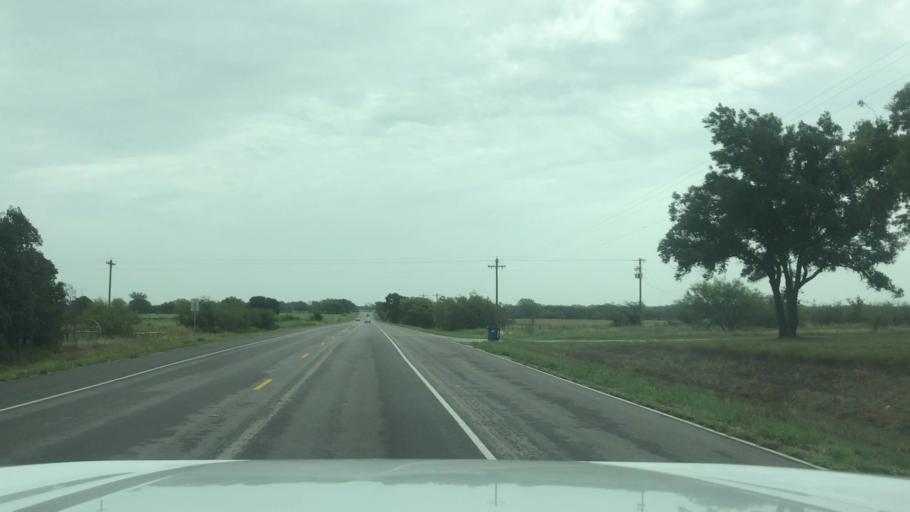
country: US
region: Texas
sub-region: Eastland County
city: Gorman
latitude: 32.2218
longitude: -98.6956
